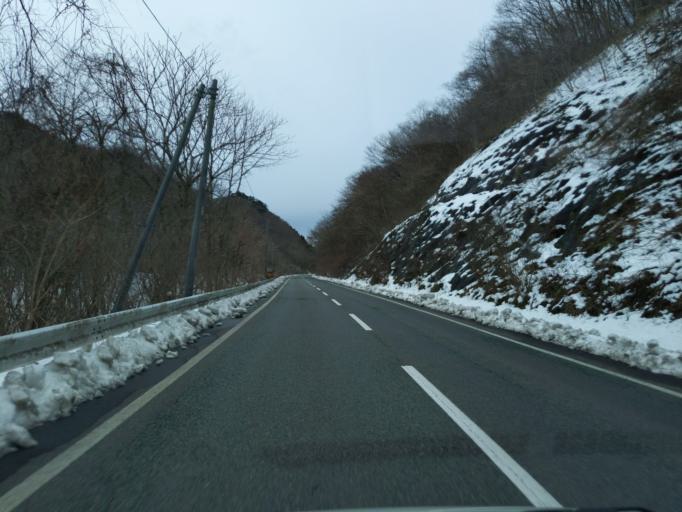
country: JP
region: Iwate
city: Mizusawa
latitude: 39.0951
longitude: 141.2686
